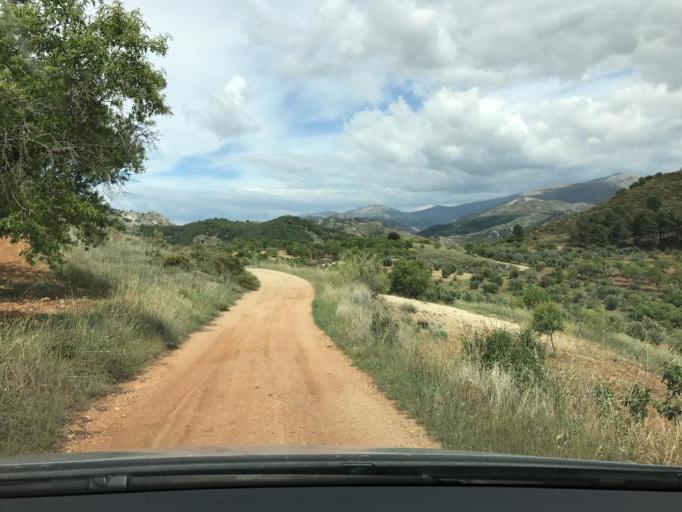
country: ES
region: Andalusia
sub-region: Provincia de Granada
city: Beas de Granada
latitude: 37.2167
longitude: -3.4606
